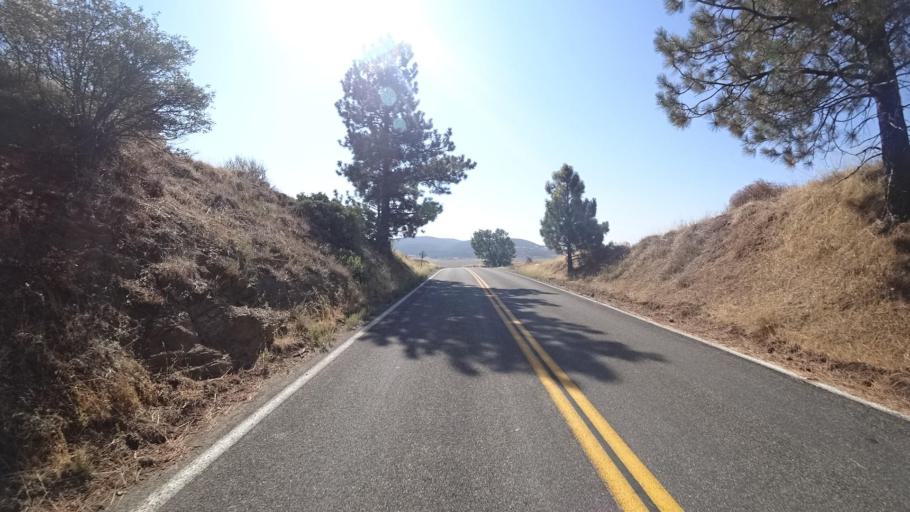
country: US
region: California
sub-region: San Diego County
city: Julian
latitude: 33.0056
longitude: -116.5563
